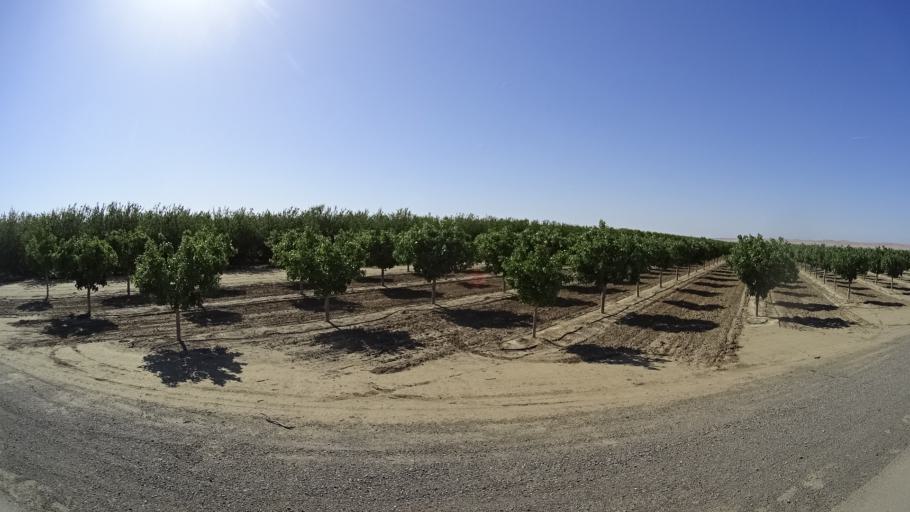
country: US
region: California
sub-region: Fresno County
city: Huron
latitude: 36.1294
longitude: -120.0220
